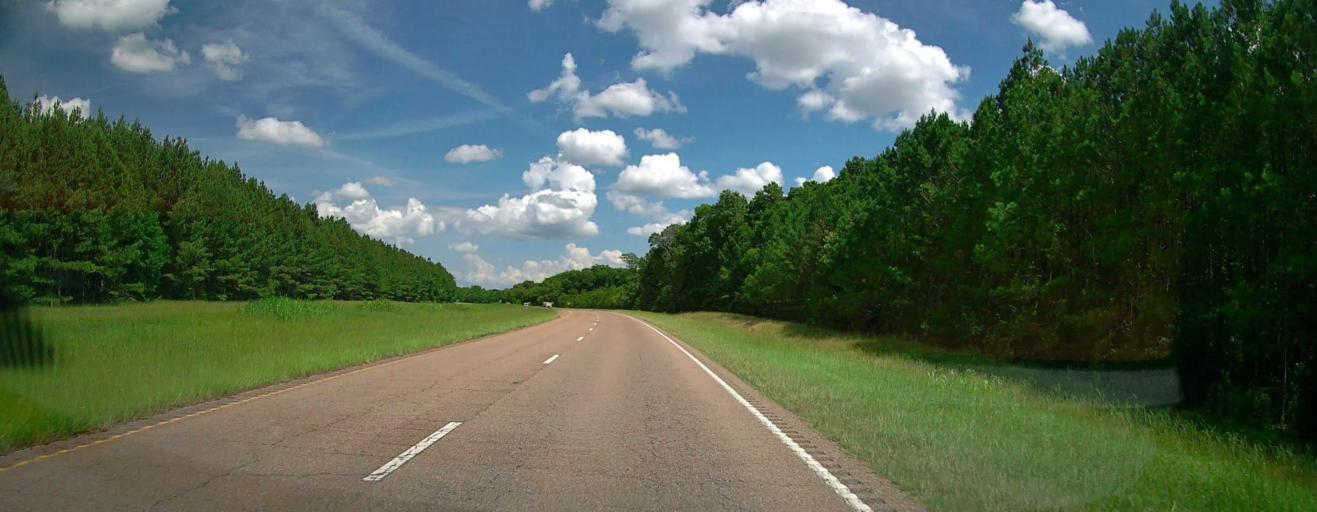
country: US
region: Mississippi
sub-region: Monroe County
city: Aberdeen
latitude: 33.8167
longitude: -88.5776
